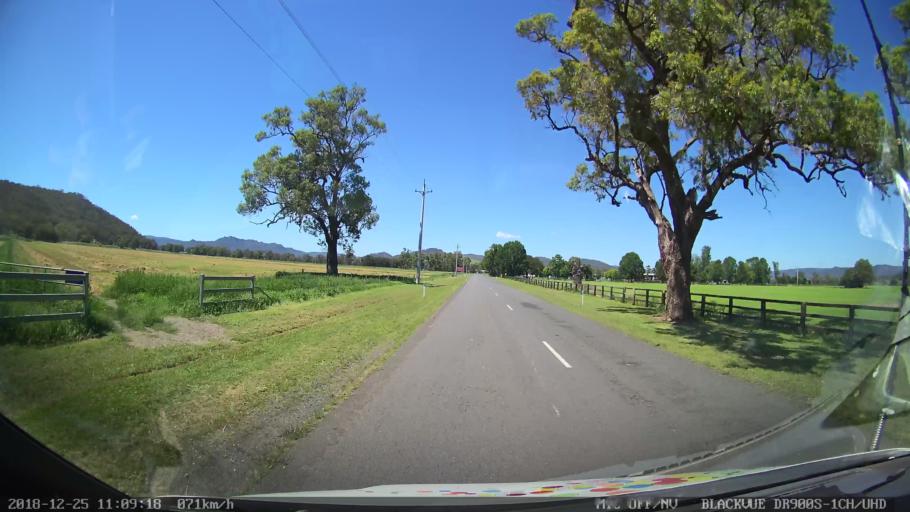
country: AU
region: New South Wales
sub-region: Upper Hunter Shire
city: Merriwa
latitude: -32.4099
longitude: 150.1191
